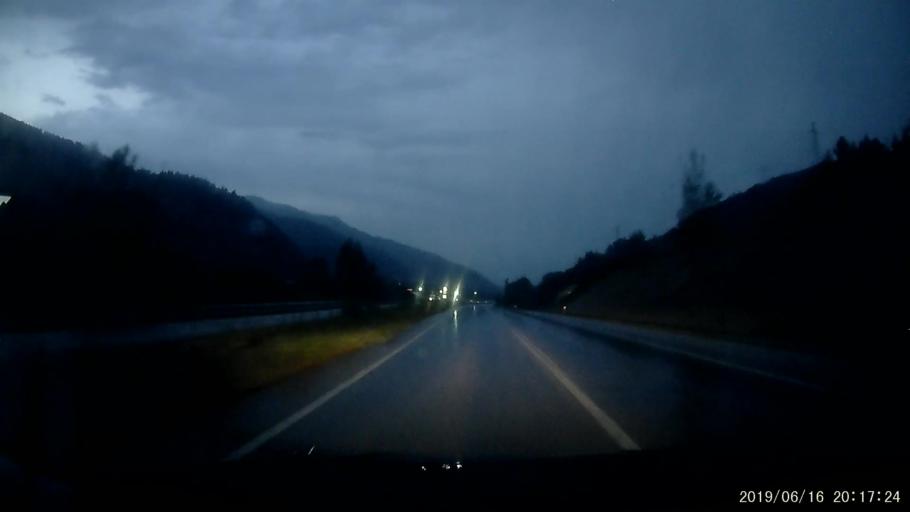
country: TR
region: Tokat
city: Resadiye
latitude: 40.3650
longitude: 37.4234
